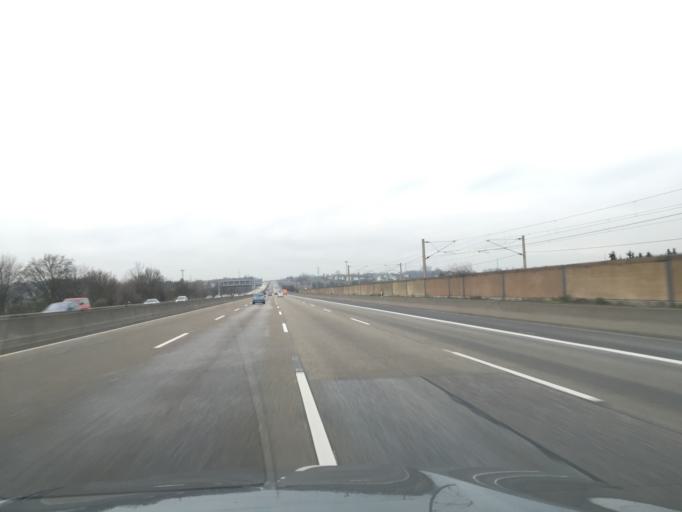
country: DE
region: Hesse
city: Raunheim
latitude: 50.0337
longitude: 8.4459
